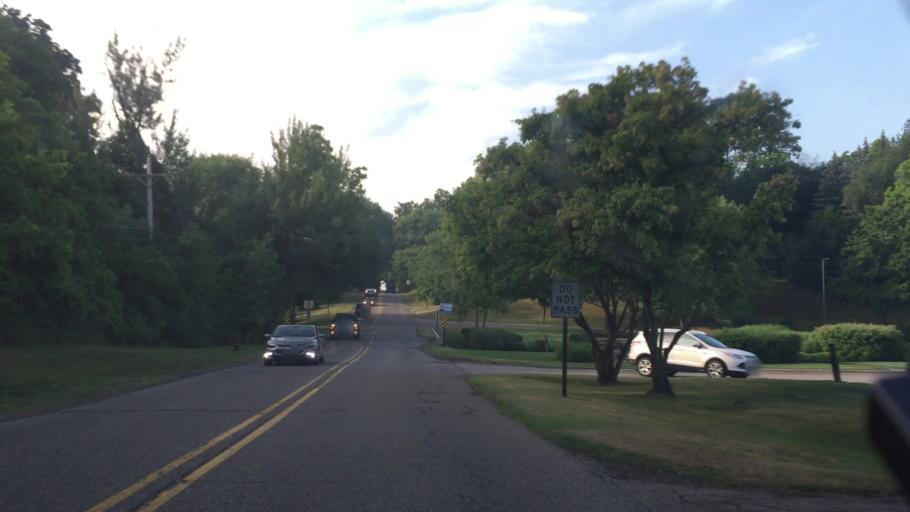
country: US
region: Michigan
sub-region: Oakland County
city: Bloomfield Hills
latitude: 42.5929
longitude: -83.2475
